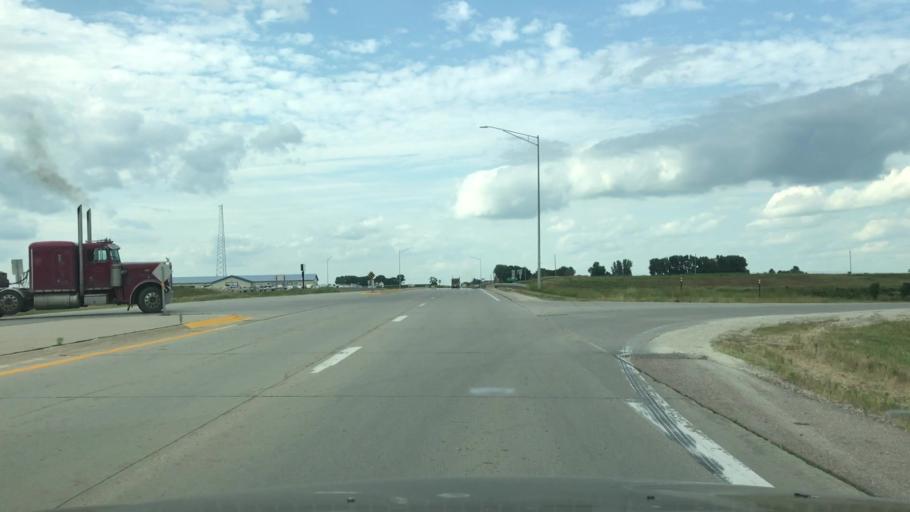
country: US
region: Iowa
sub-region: Plymouth County
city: Le Mars
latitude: 42.8164
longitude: -96.1746
